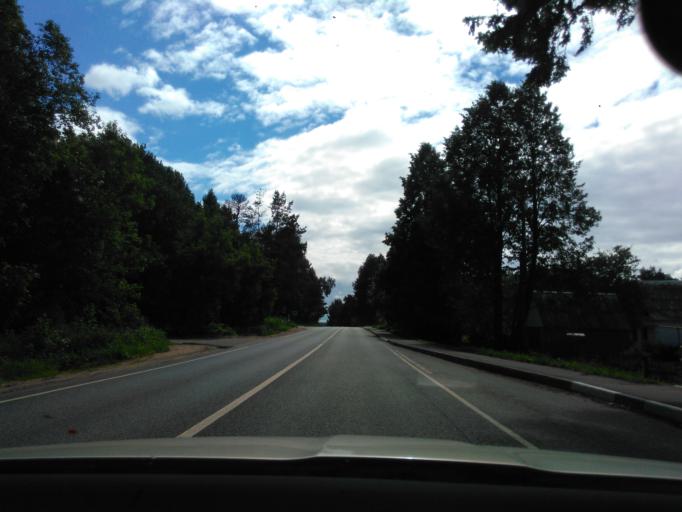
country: RU
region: Moskovskaya
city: Shevlyakovo
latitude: 56.4145
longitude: 36.8750
